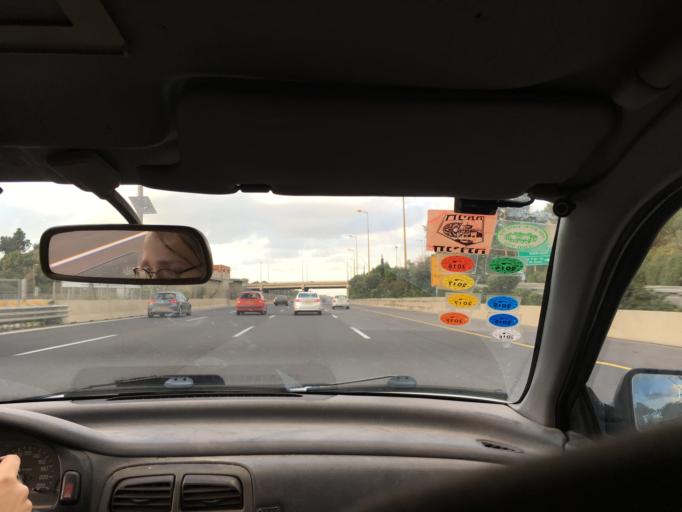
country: IL
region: Tel Aviv
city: Ramat Gan
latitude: 32.1161
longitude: 34.8109
